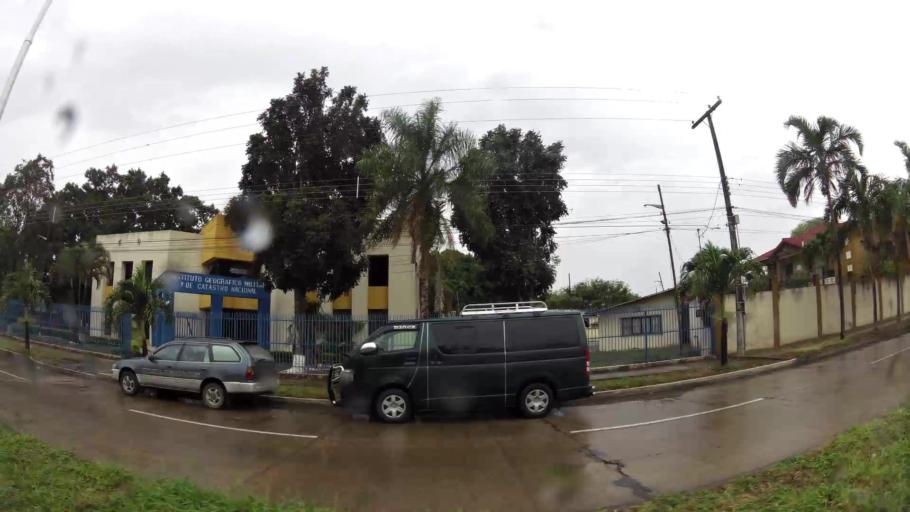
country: BO
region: Santa Cruz
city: Santa Cruz de la Sierra
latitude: -17.7970
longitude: -63.1599
